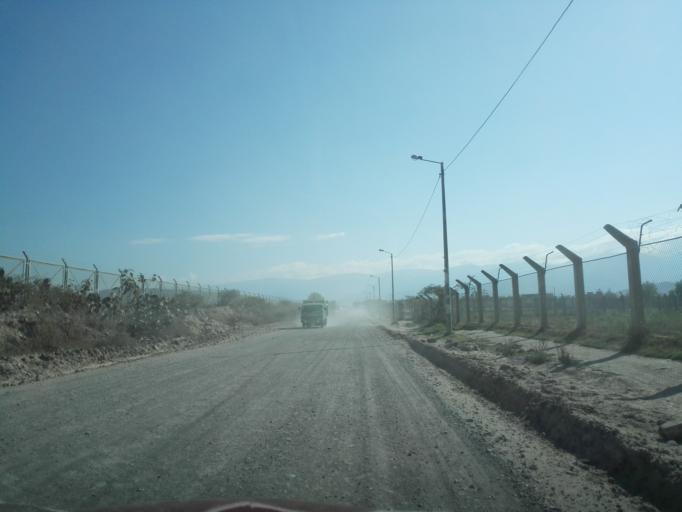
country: PE
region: Ayacucho
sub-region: Provincia de Huamanga
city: Ayacucho
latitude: -13.1627
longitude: -74.2071
